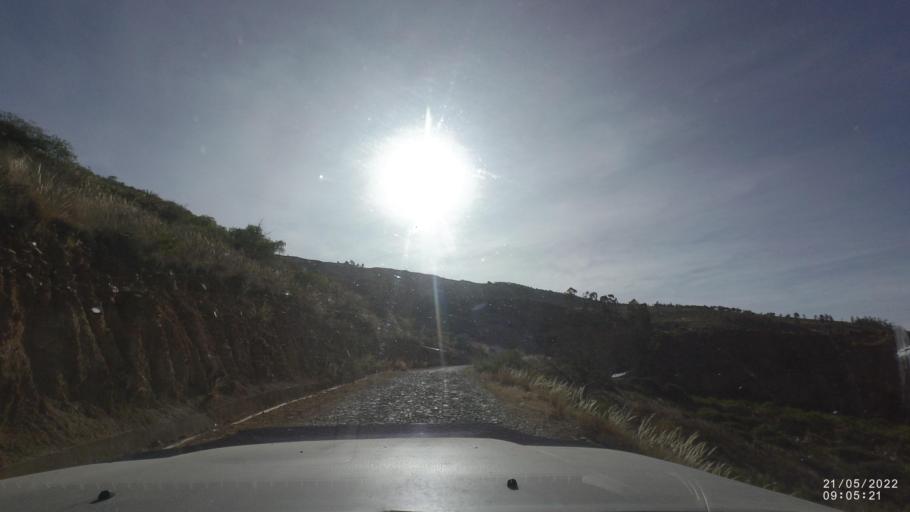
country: BO
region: Cochabamba
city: Cochabamba
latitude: -17.3795
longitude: -66.0227
